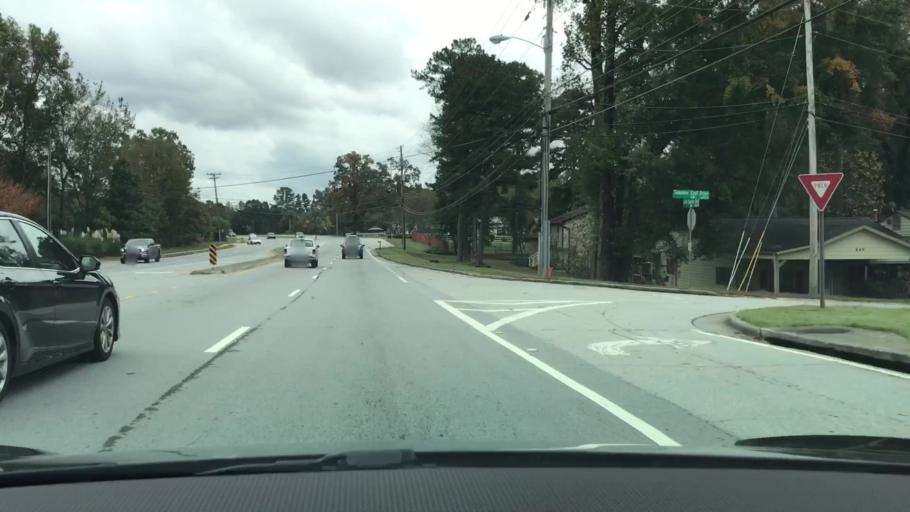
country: US
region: Georgia
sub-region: Gwinnett County
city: Lawrenceville
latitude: 33.9960
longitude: -84.0356
